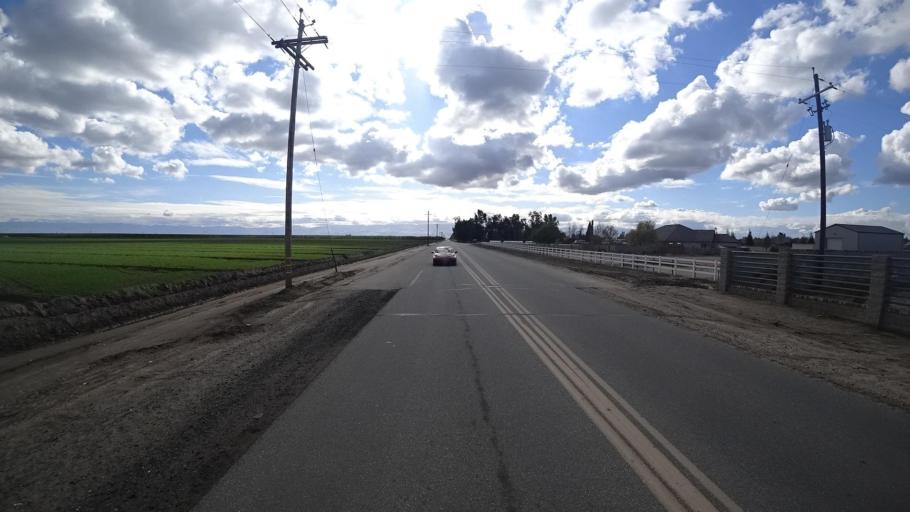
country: US
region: California
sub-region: Kern County
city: Greenfield
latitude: 35.2362
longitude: -119.0740
